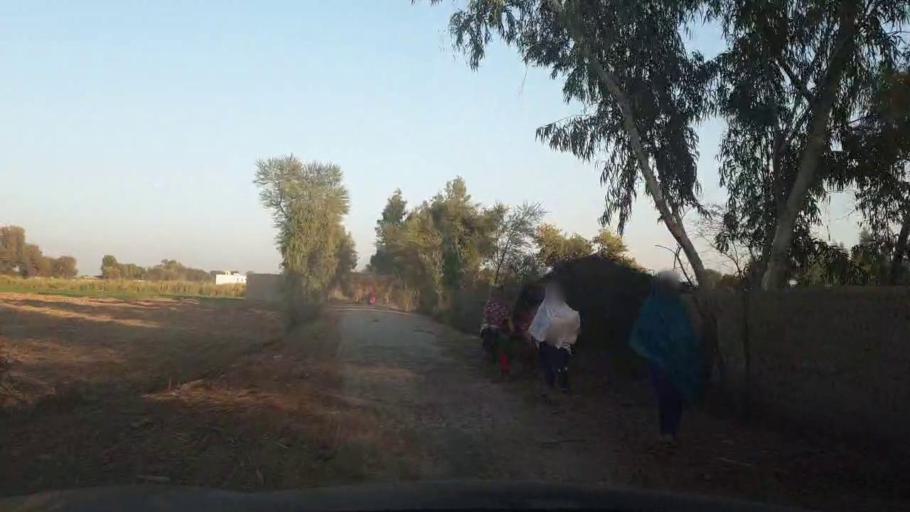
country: PK
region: Sindh
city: Ubauro
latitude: 28.1712
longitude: 69.5875
